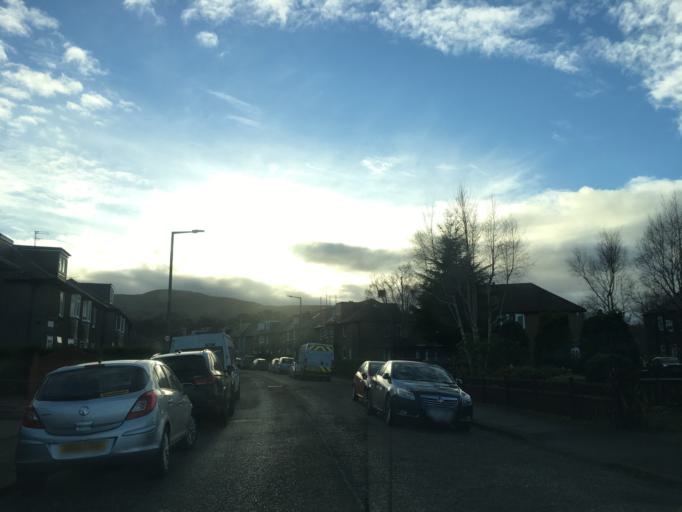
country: GB
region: Scotland
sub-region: Edinburgh
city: Colinton
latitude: 55.9096
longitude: -3.2342
